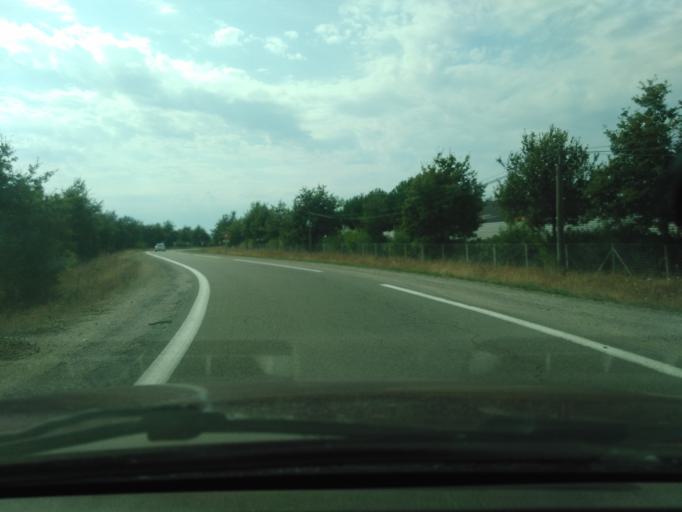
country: FR
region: Pays de la Loire
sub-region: Departement de la Vendee
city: Mouilleron-le-Captif
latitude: 46.7451
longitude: -1.4275
